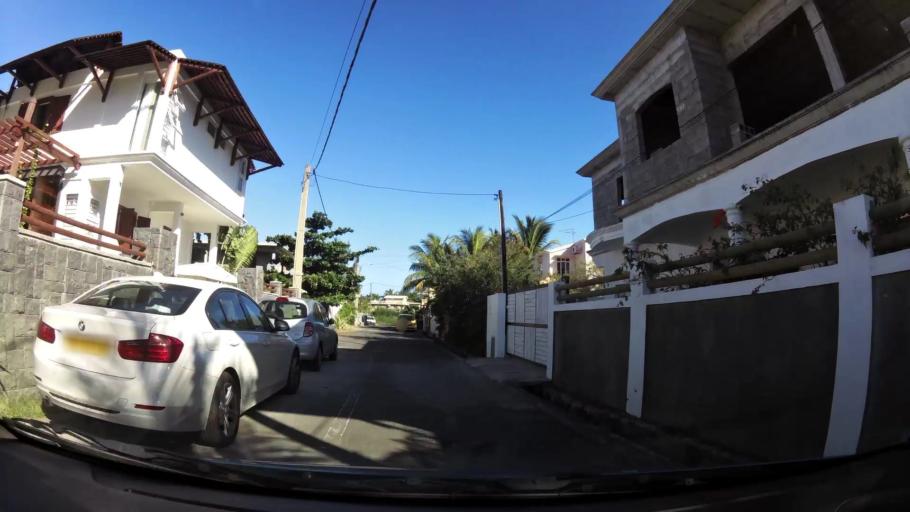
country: MU
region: Black River
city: Grande Riviere Noire
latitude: -20.3539
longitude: 57.3640
